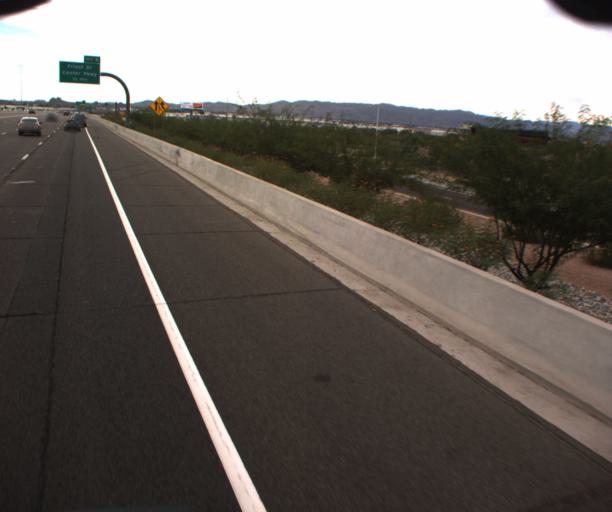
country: US
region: Arizona
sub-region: Maricopa County
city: Tempe Junction
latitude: 33.4497
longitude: -111.9691
